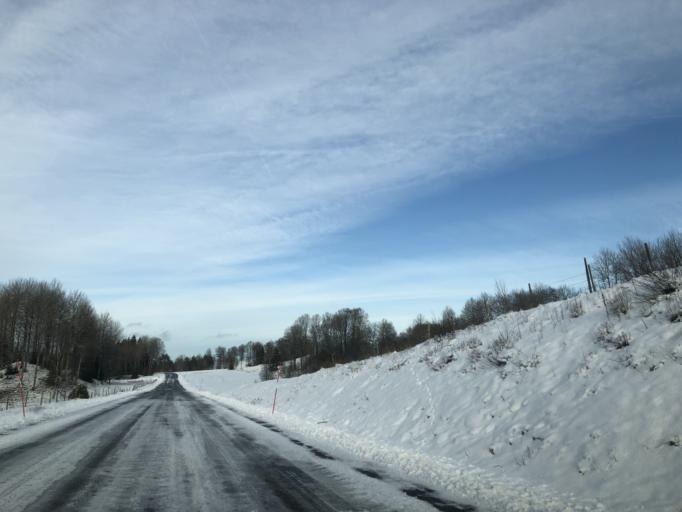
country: SE
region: Vaestra Goetaland
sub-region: Ulricehamns Kommun
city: Ulricehamn
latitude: 57.8009
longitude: 13.5419
